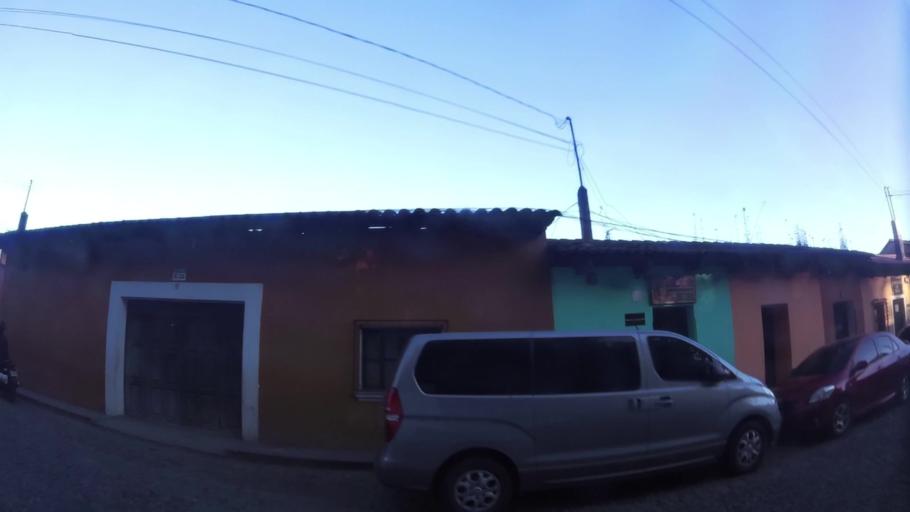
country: GT
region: Sacatepequez
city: Antigua Guatemala
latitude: 14.5616
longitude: -90.7373
